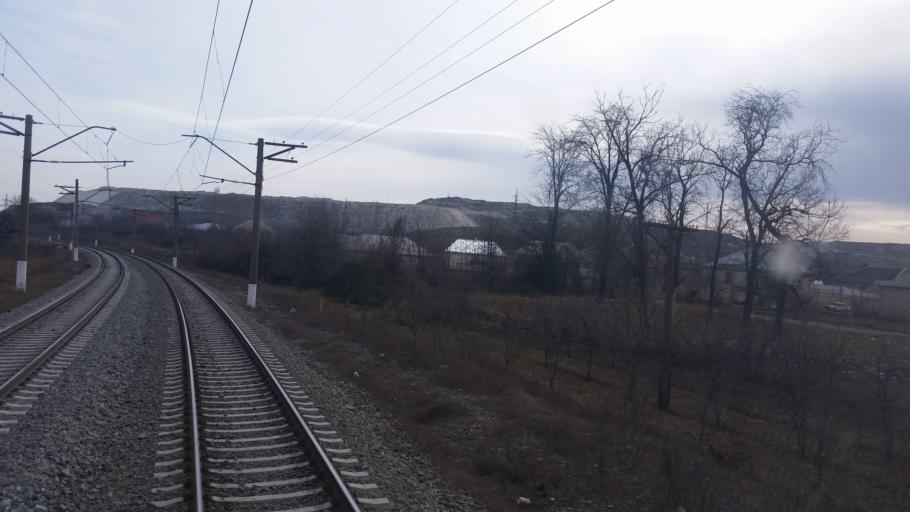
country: AZ
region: Shamkir Rayon
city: Dzagam
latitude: 40.9100
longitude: 45.8448
